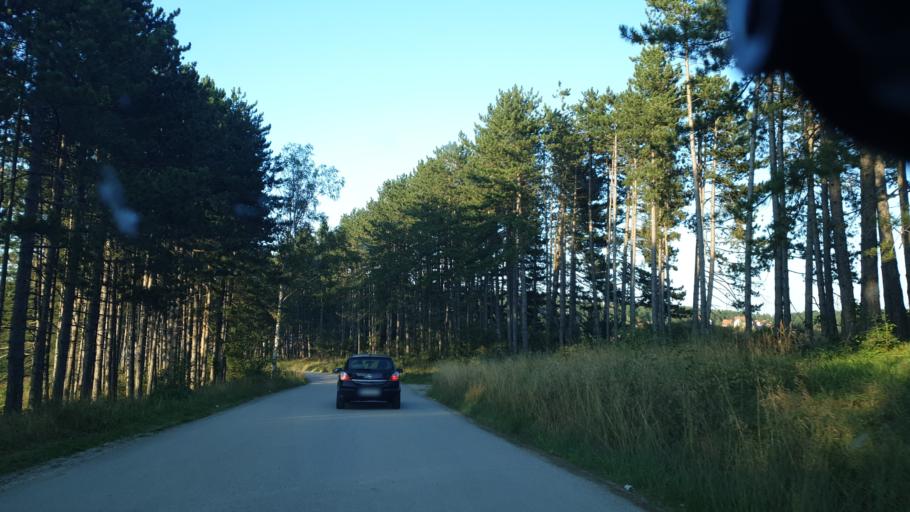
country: RS
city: Zlatibor
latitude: 43.7159
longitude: 19.6911
